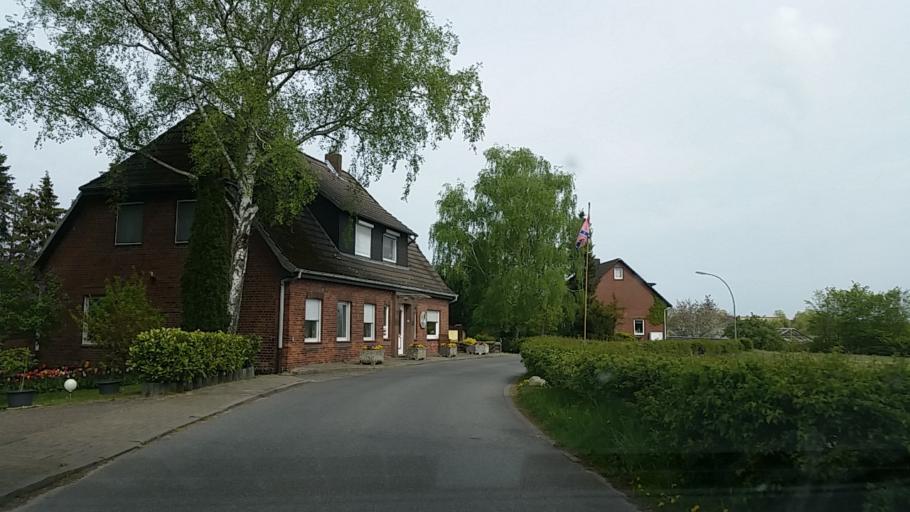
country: DE
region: Hamburg
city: Rothenburgsort
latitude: 53.4780
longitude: 10.0869
